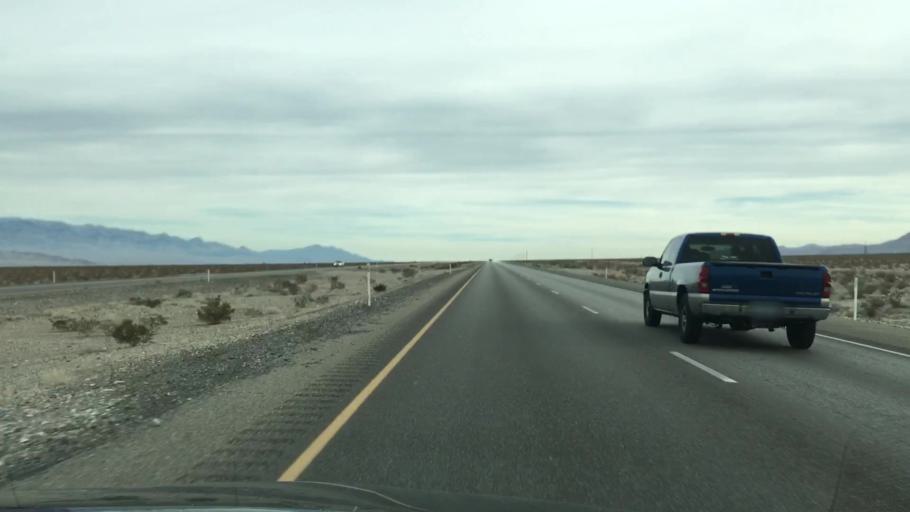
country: US
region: Nevada
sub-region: Nye County
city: Pahrump
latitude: 36.5714
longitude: -115.6309
